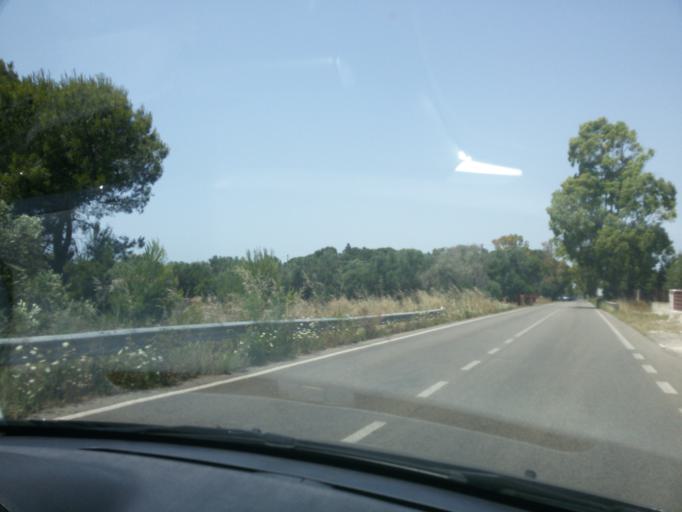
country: IT
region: Apulia
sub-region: Provincia di Lecce
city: Porto Cesareo
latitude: 40.2596
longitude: 17.9227
